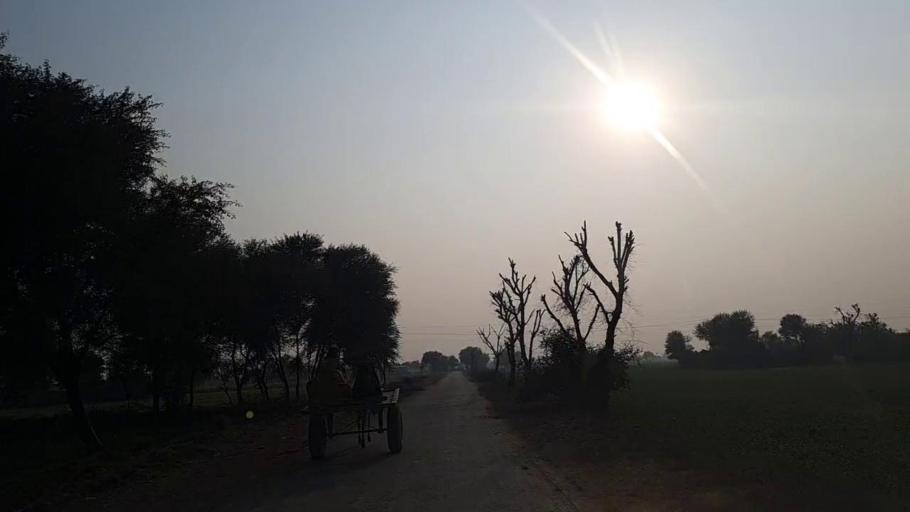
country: PK
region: Sindh
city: Nawabshah
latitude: 26.2276
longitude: 68.4821
